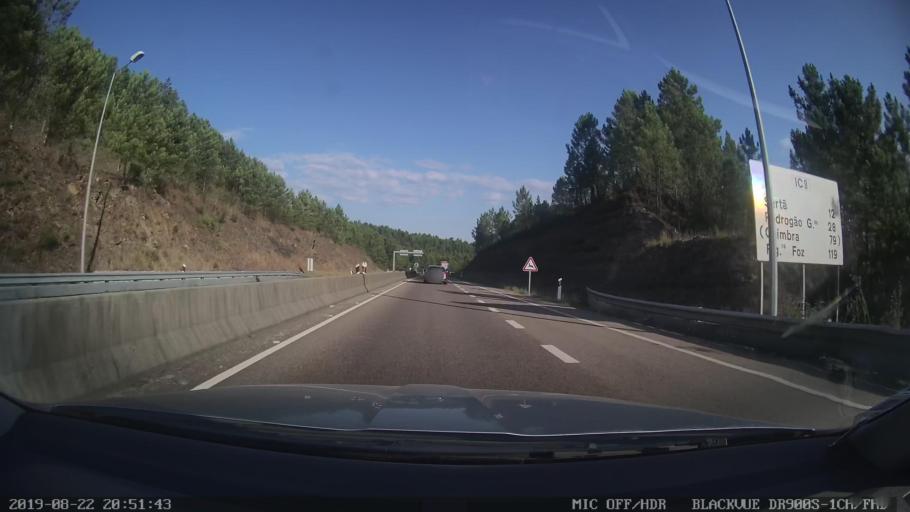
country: PT
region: Castelo Branco
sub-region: Proenca-A-Nova
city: Proenca-a-Nova
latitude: 39.7619
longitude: -7.9646
